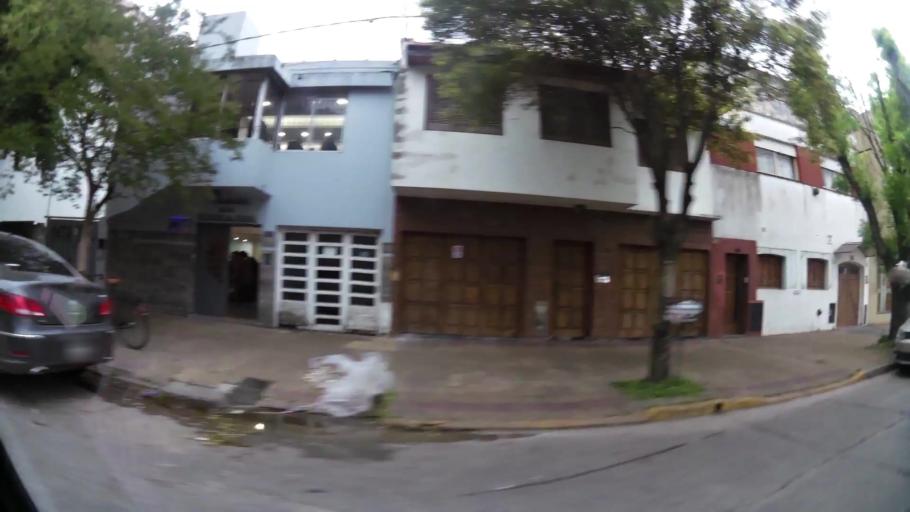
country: AR
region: Buenos Aires
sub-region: Partido de La Plata
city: La Plata
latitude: -34.9180
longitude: -57.9758
